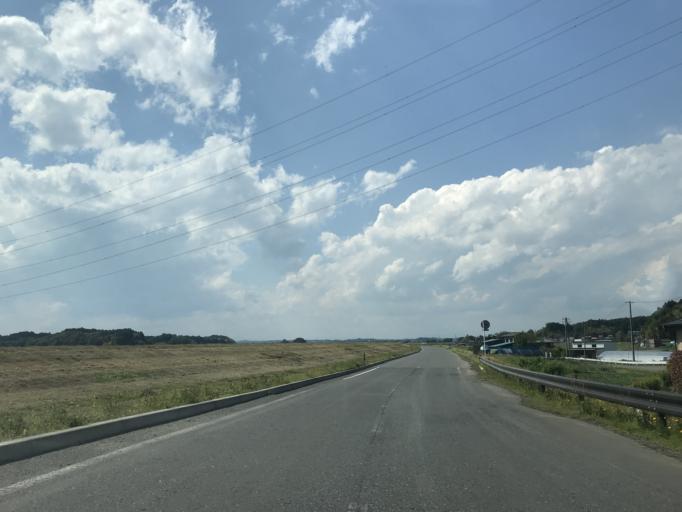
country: JP
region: Miyagi
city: Matsushima
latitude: 38.4298
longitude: 141.1244
